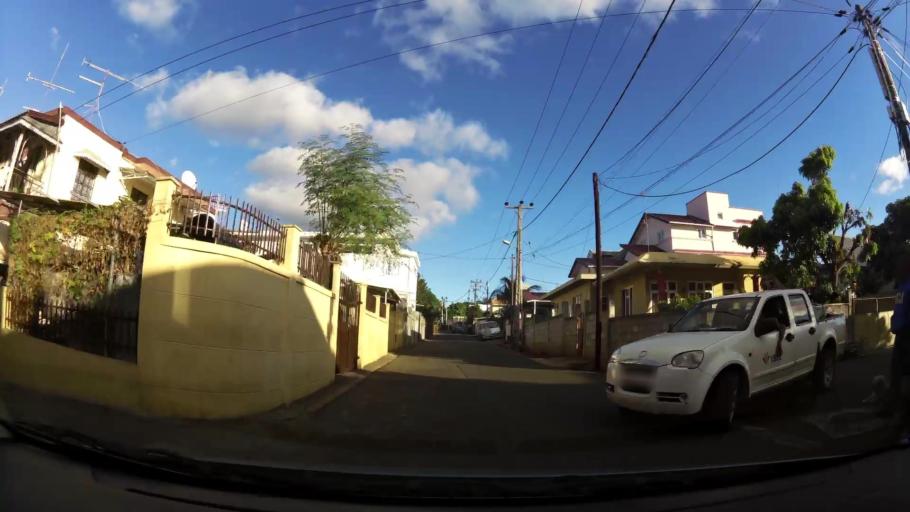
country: MU
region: Black River
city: Petite Riviere
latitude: -20.2178
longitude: 57.4622
